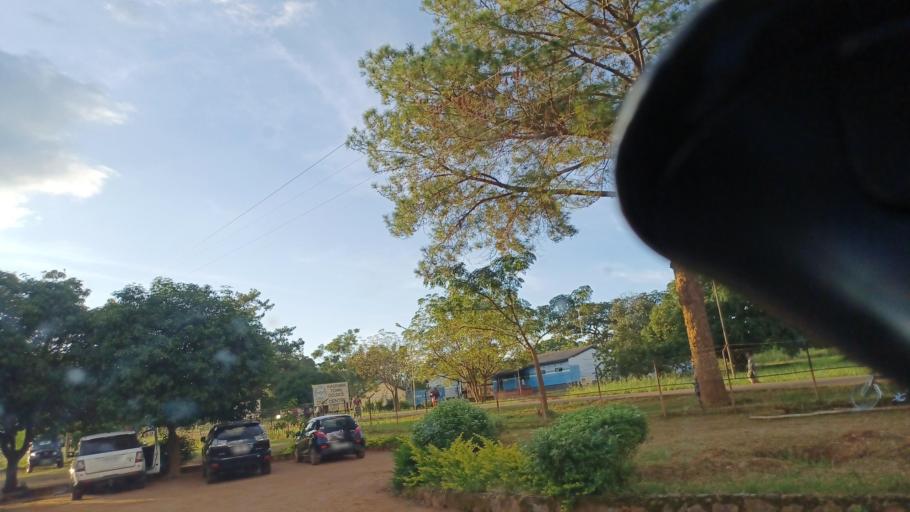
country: ZM
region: North-Western
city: Kasempa
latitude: -13.4578
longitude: 25.8317
